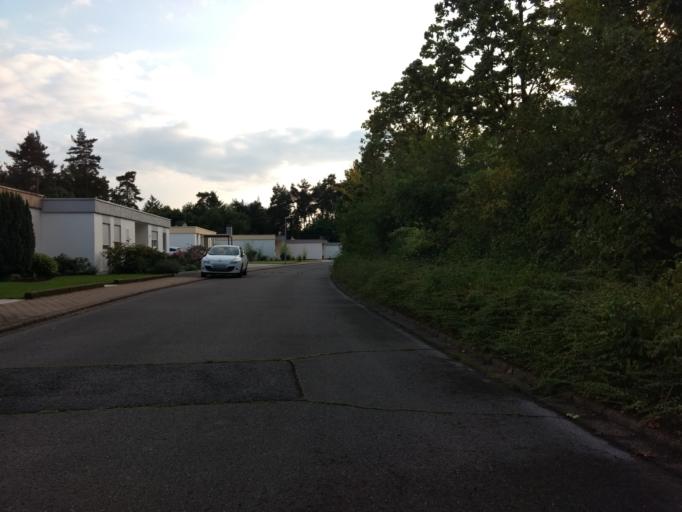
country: DE
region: Saarland
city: Dillingen
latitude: 49.3735
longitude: 6.7276
